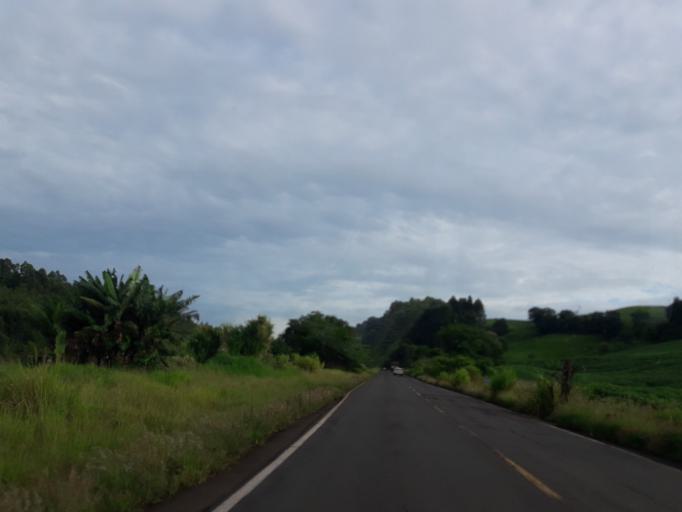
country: AR
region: Misiones
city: Bernardo de Irigoyen
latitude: -26.3632
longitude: -53.5347
